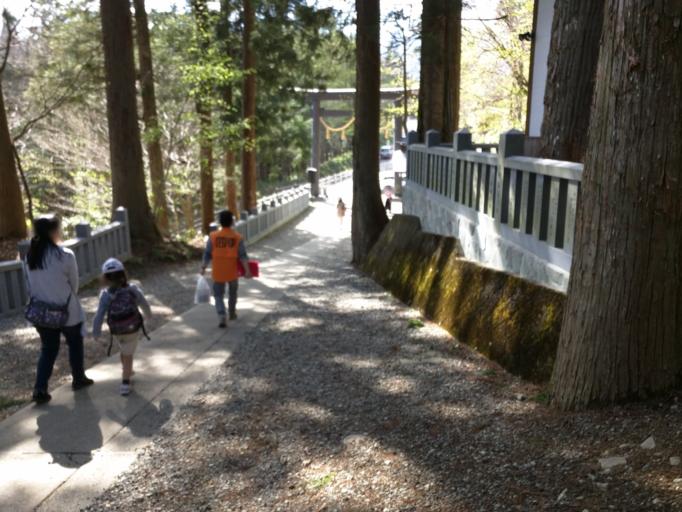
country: JP
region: Nagano
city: Nagano-shi
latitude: 36.7425
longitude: 138.0846
